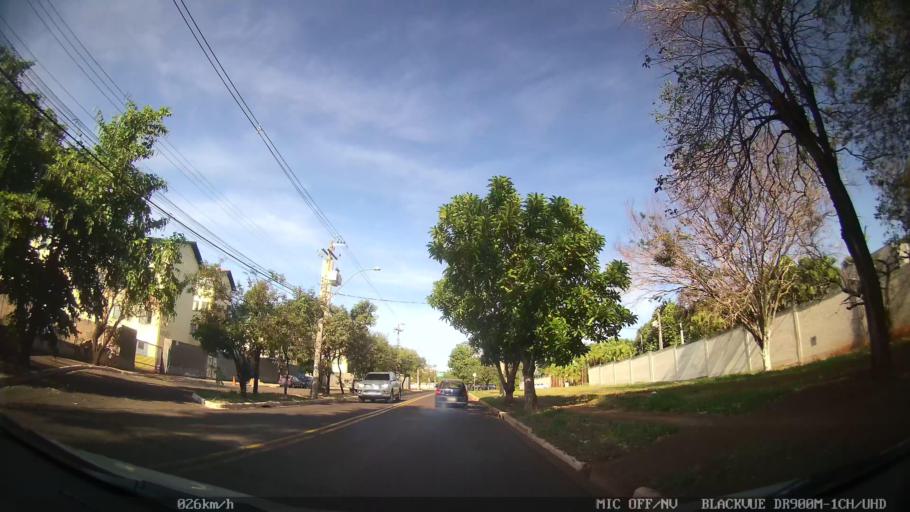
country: BR
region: Sao Paulo
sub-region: Ribeirao Preto
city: Ribeirao Preto
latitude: -21.2120
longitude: -47.8269
